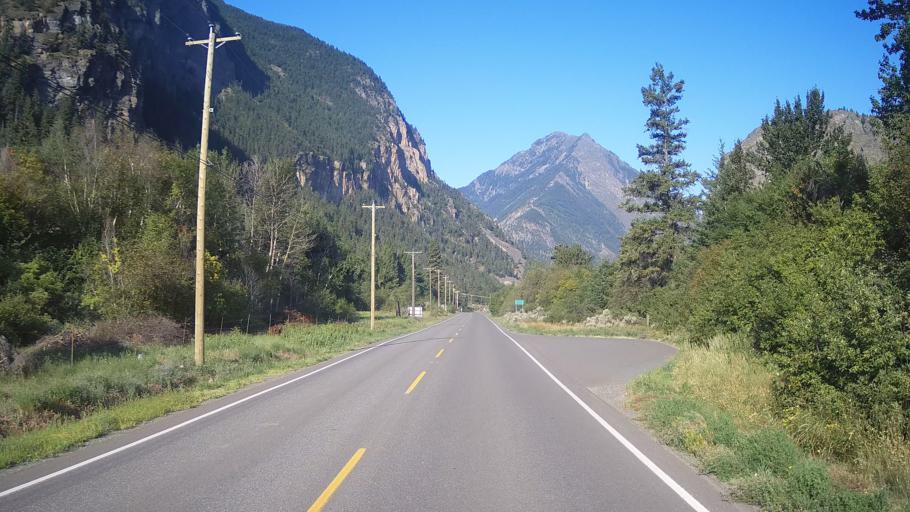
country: CA
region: British Columbia
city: Lillooet
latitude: 50.6718
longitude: -121.9427
